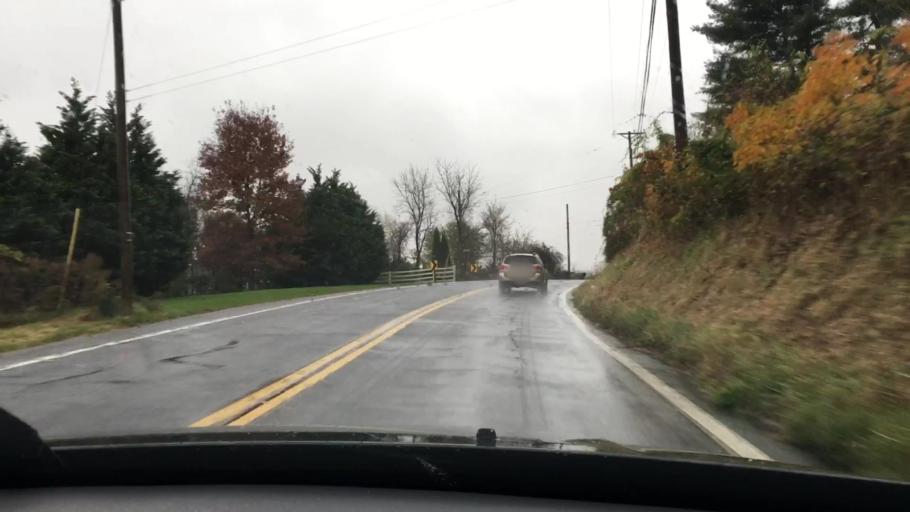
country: US
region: Maryland
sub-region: Carroll County
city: Manchester
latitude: 39.6970
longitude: -76.8720
